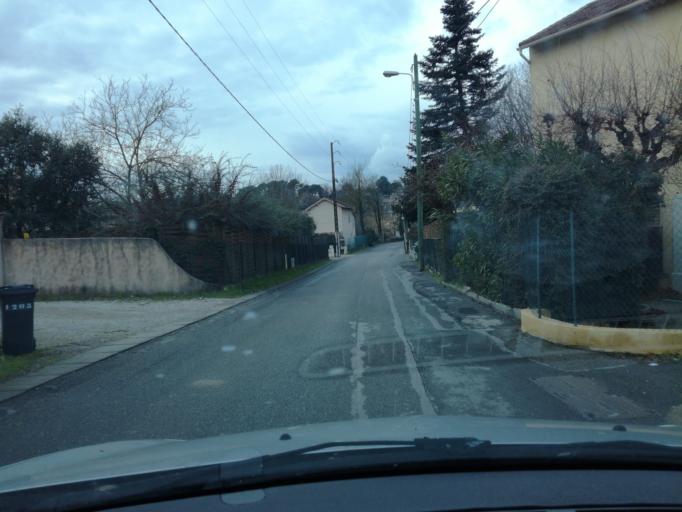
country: FR
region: Provence-Alpes-Cote d'Azur
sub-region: Departement des Alpes-Maritimes
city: Mouans-Sartoux
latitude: 43.6055
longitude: 6.9756
